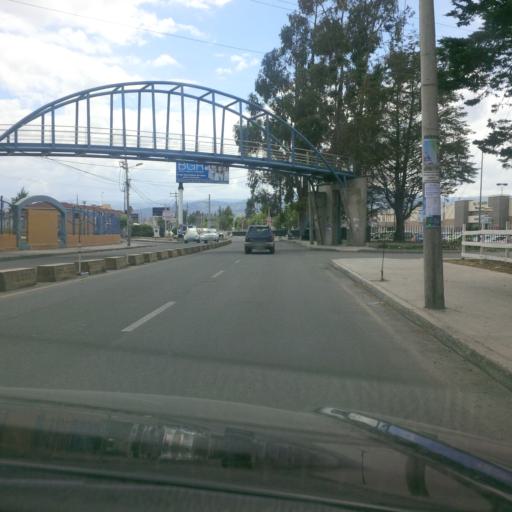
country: EC
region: Chimborazo
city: Riobamba
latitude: -1.6532
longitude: -78.6444
